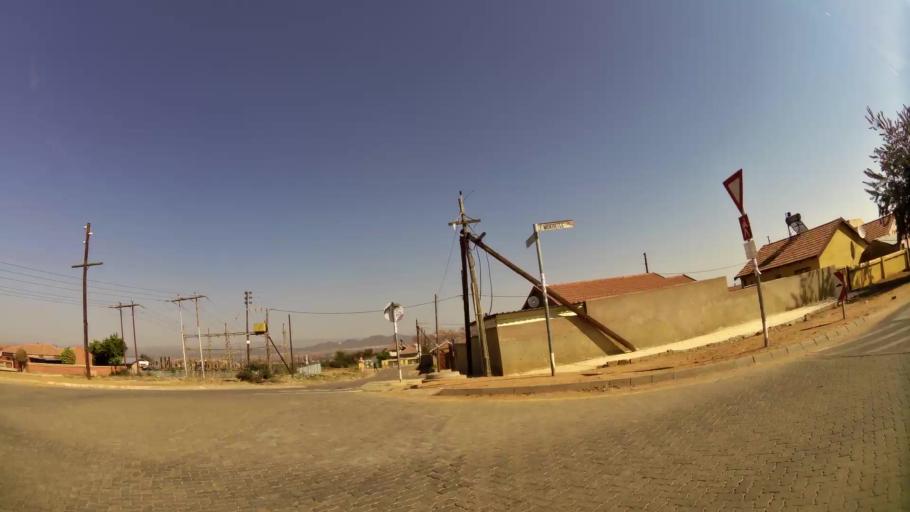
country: ZA
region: Gauteng
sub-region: City of Tshwane Metropolitan Municipality
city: Mabopane
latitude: -25.5587
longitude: 28.0757
